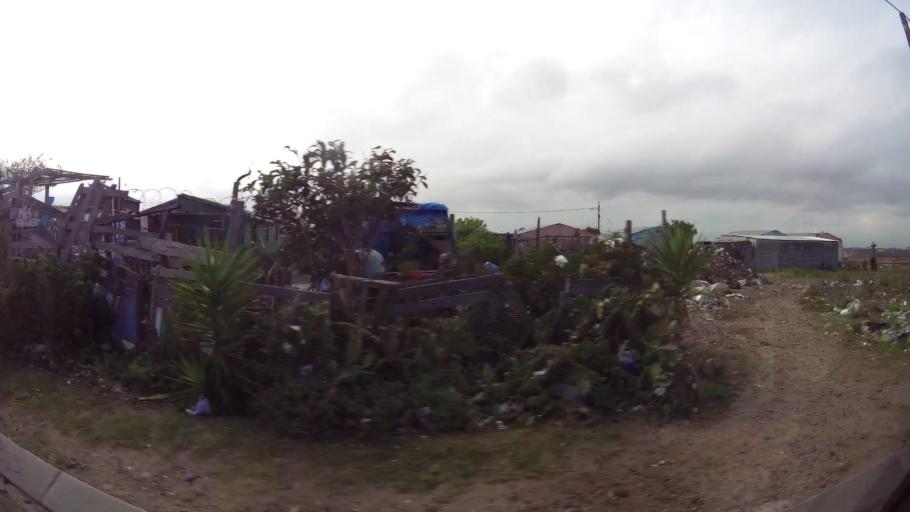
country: ZA
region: Eastern Cape
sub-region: Nelson Mandela Bay Metropolitan Municipality
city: Port Elizabeth
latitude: -33.9170
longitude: 25.5384
